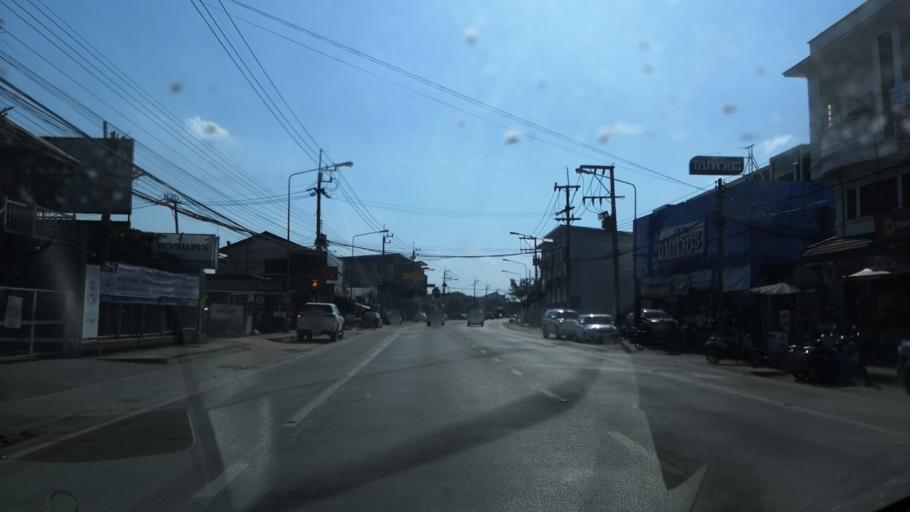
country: TH
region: Chiang Rai
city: Chiang Rai
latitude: 19.9291
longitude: 99.8388
